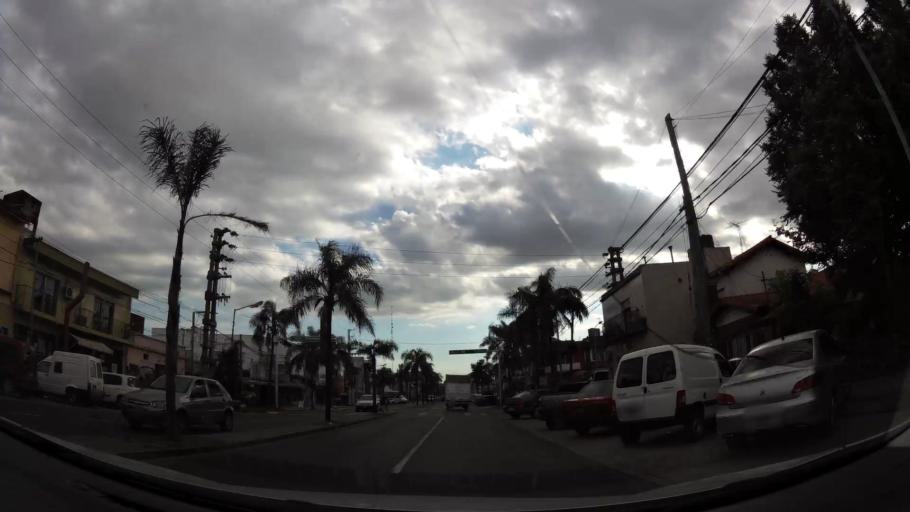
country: AR
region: Buenos Aires
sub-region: Partido de Tigre
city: Tigre
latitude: -34.4672
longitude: -58.6470
